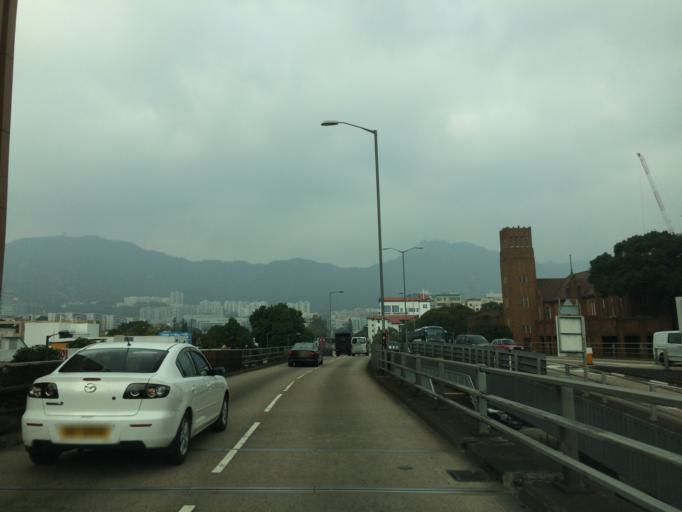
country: HK
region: Kowloon City
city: Kowloon
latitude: 22.3265
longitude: 114.1783
